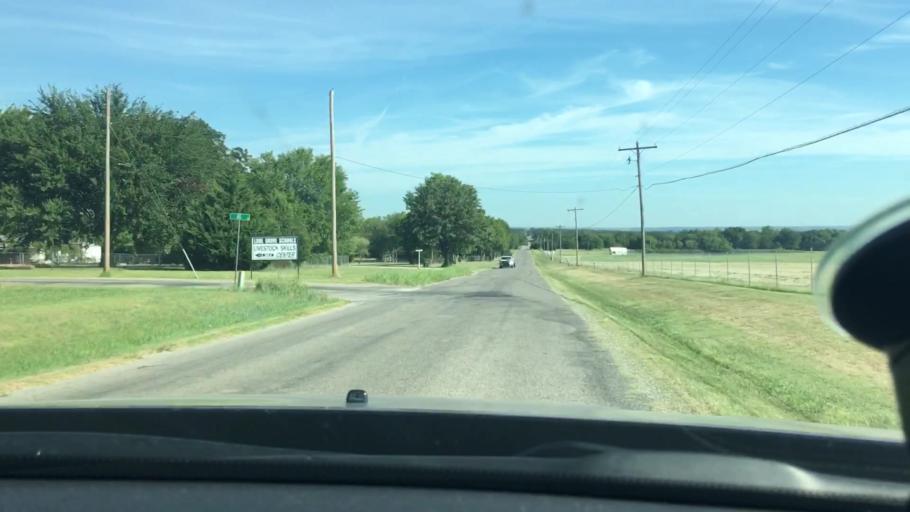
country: US
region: Oklahoma
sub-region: Carter County
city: Lone Grove
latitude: 34.2252
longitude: -97.2474
